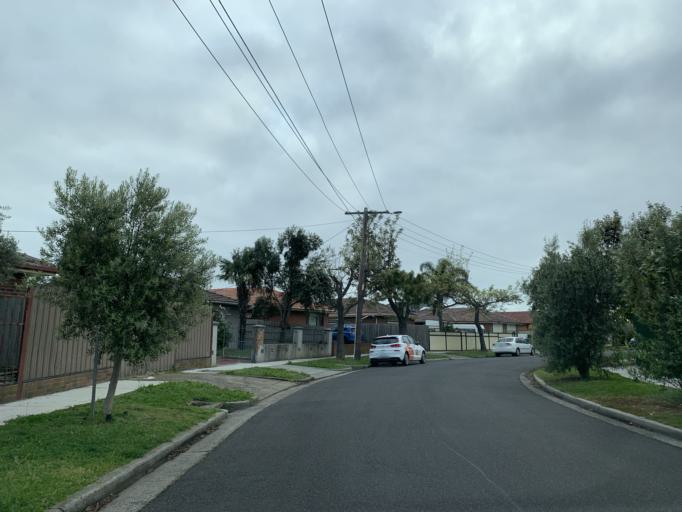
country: AU
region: Victoria
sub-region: Brimbank
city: Kealba
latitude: -37.7500
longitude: 144.8211
